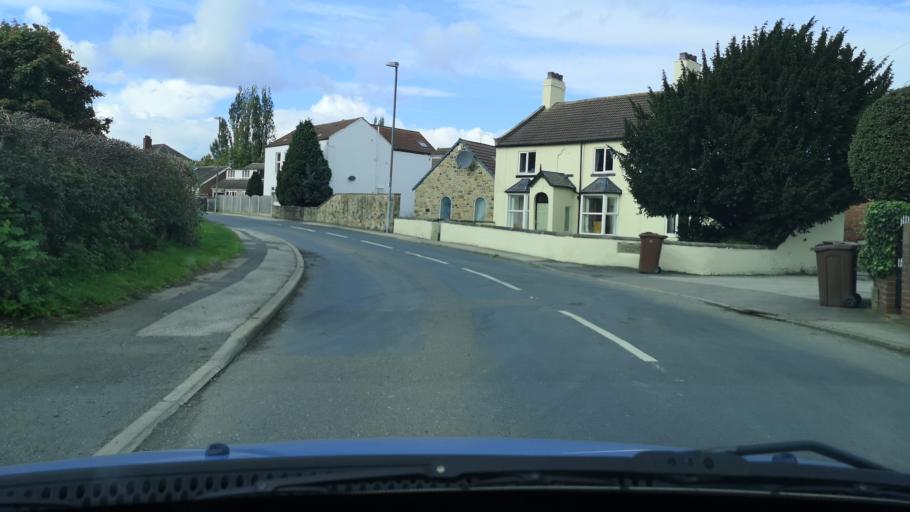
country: GB
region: England
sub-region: City and Borough of Wakefield
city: Normanton
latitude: 53.6883
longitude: -1.3936
